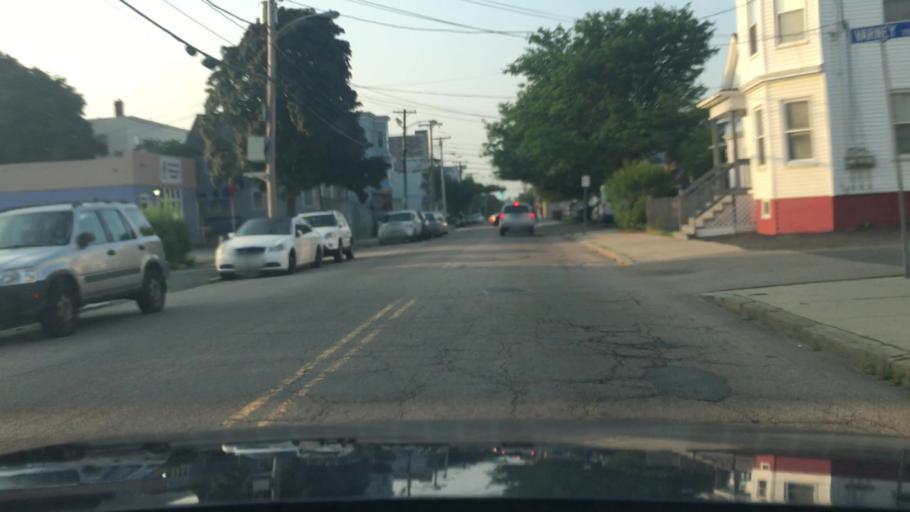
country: US
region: Massachusetts
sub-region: Essex County
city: Lynn
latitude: 42.4617
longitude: -70.9618
